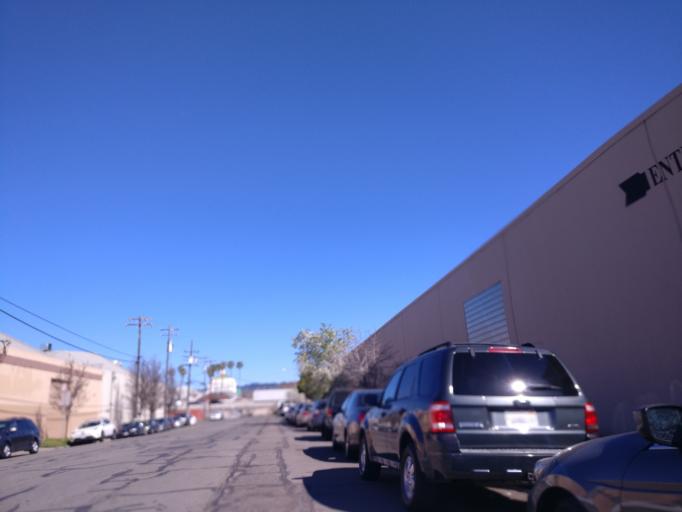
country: US
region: California
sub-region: Alameda County
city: Oakland
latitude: 37.7931
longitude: -122.2663
